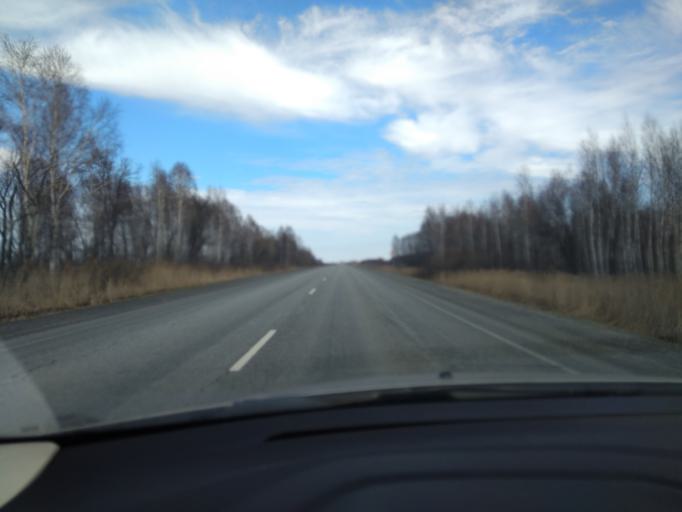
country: RU
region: Sverdlovsk
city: Pyshma
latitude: 57.0071
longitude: 63.3370
